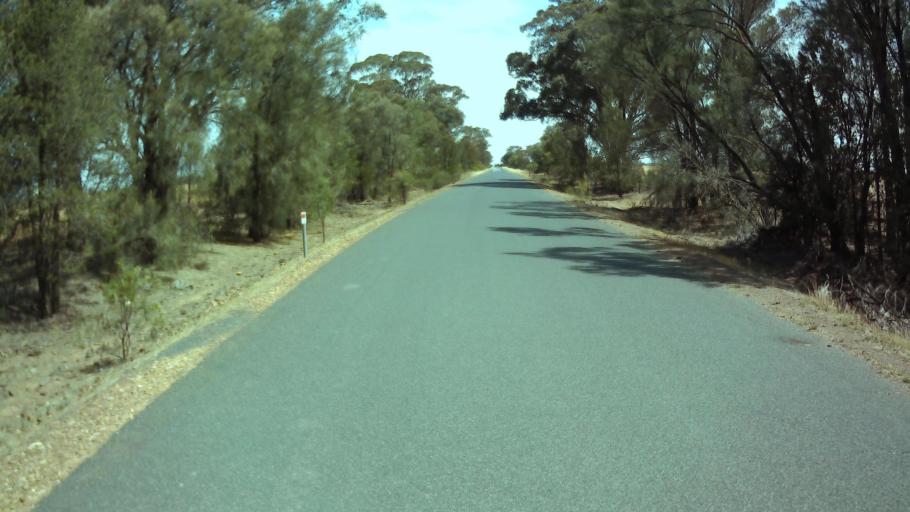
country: AU
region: New South Wales
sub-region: Weddin
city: Grenfell
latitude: -33.9464
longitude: 147.7787
